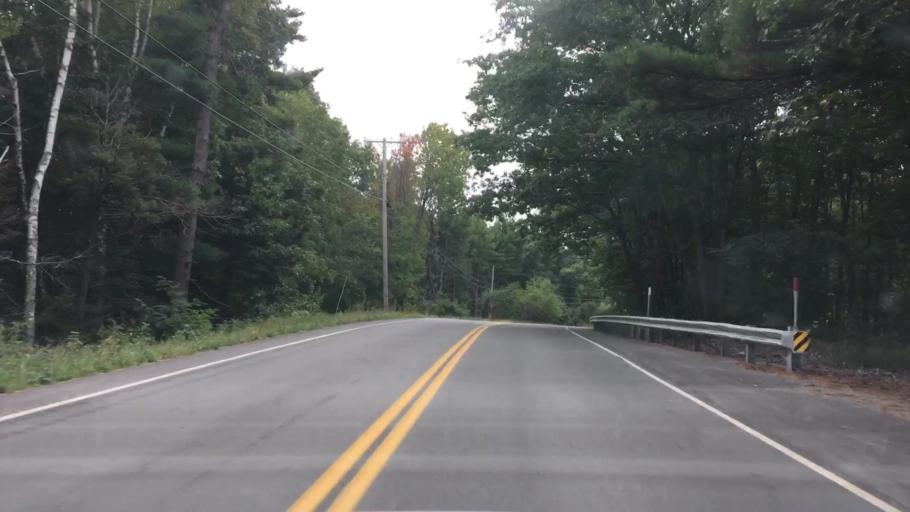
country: US
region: Maine
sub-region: Penobscot County
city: Milford
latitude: 44.9561
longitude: -68.6980
